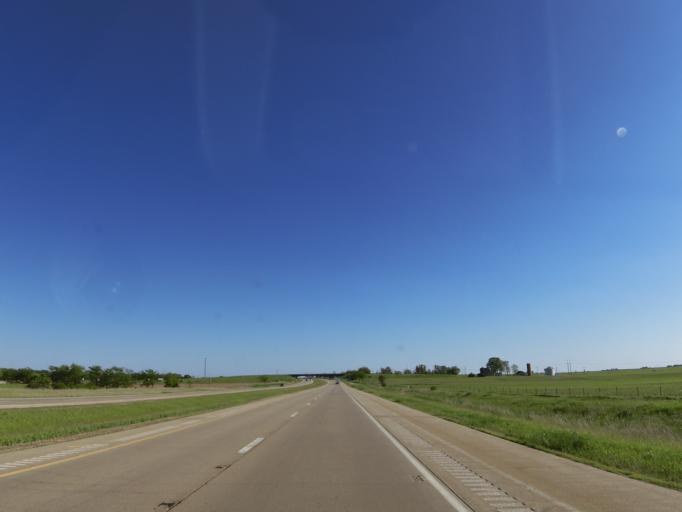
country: US
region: Illinois
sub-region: Marshall County
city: Wenona
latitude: 41.0628
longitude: -89.0673
